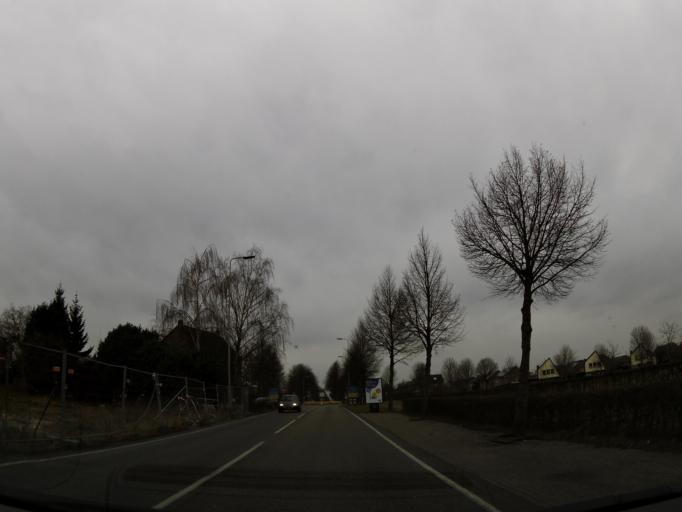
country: NL
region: Limburg
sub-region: Gemeente Schinnen
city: Doenrade
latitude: 50.9961
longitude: 5.9040
